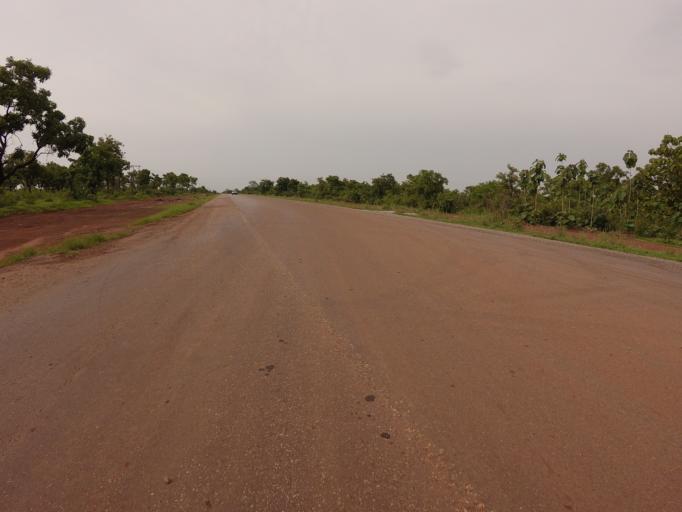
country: GH
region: Northern
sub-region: Yendi
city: Yendi
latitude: 9.6479
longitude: -0.0689
